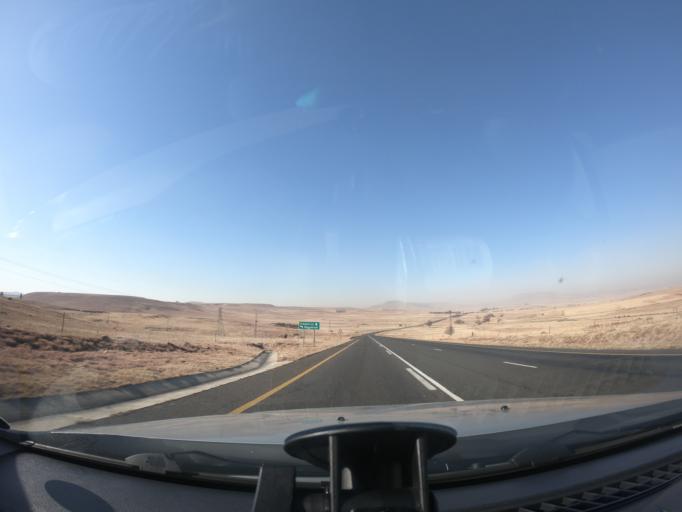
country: ZA
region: Mpumalanga
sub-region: Gert Sibande District Municipality
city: Volksrust
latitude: -27.2131
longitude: 29.8817
